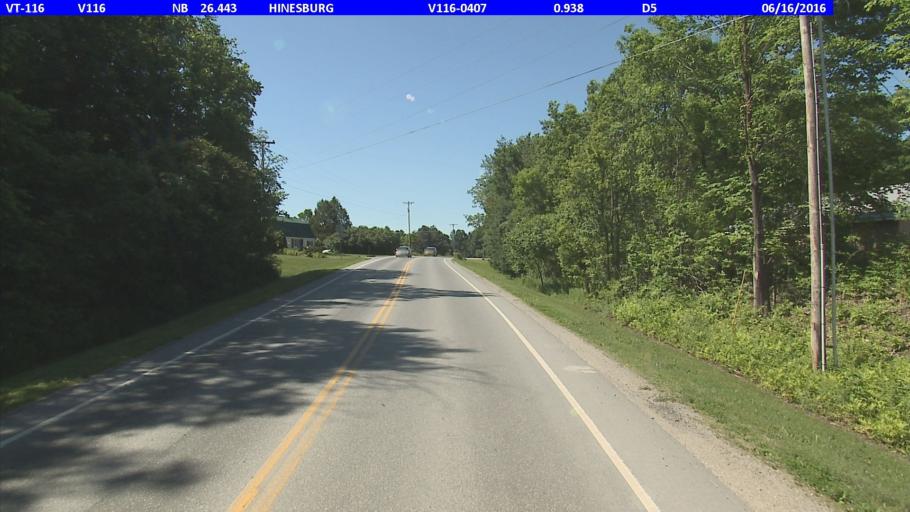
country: US
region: Vermont
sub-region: Chittenden County
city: Hinesburg
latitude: 44.2935
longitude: -73.0709
